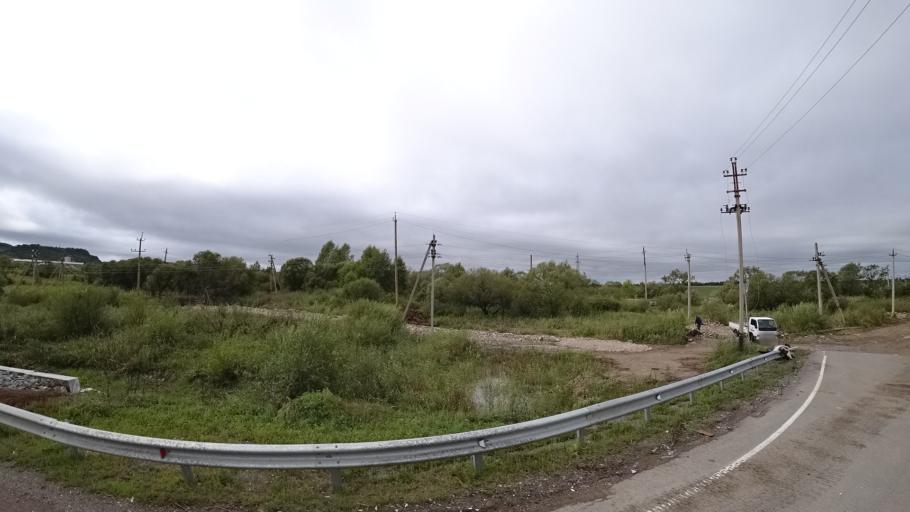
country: RU
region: Primorskiy
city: Monastyrishche
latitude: 44.1761
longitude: 132.4413
